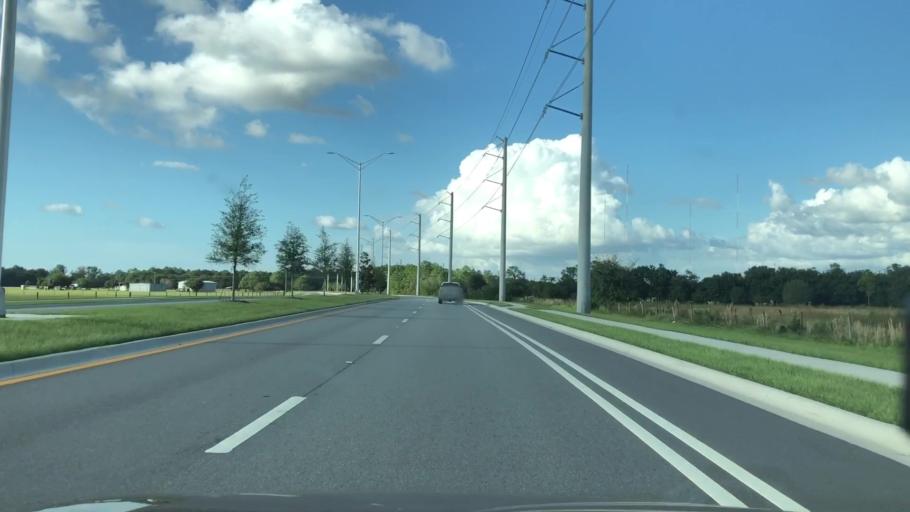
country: US
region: Florida
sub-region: Sarasota County
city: Fruitville
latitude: 27.3497
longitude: -82.3840
